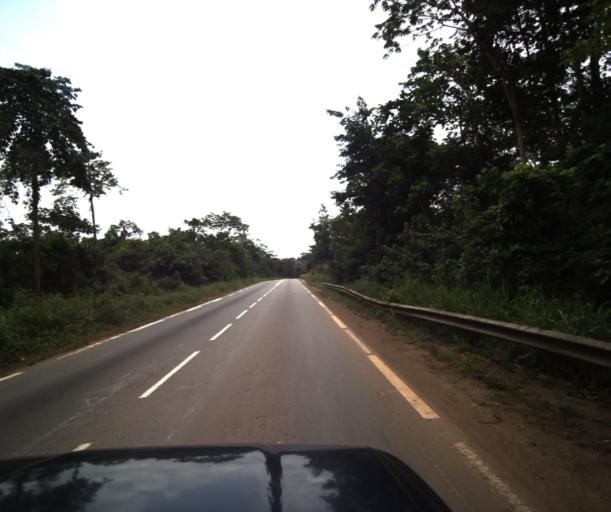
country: CM
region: Centre
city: Eseka
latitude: 3.8768
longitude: 10.8379
